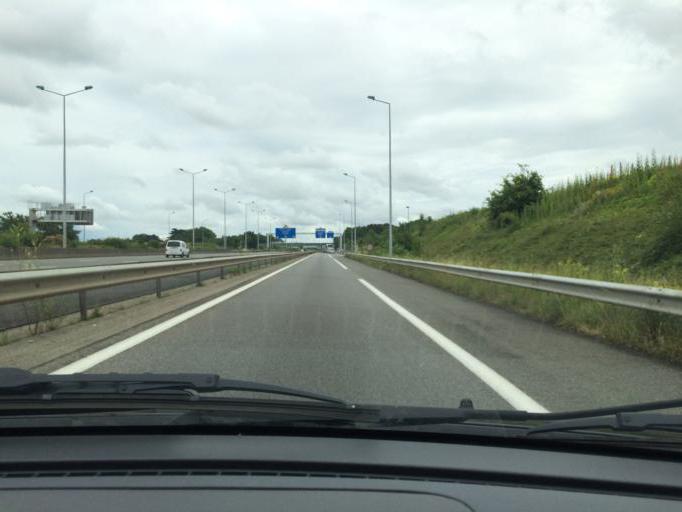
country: FR
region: Rhone-Alpes
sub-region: Departement du Rhone
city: Saint-Priest
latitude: 45.7037
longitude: 4.9639
